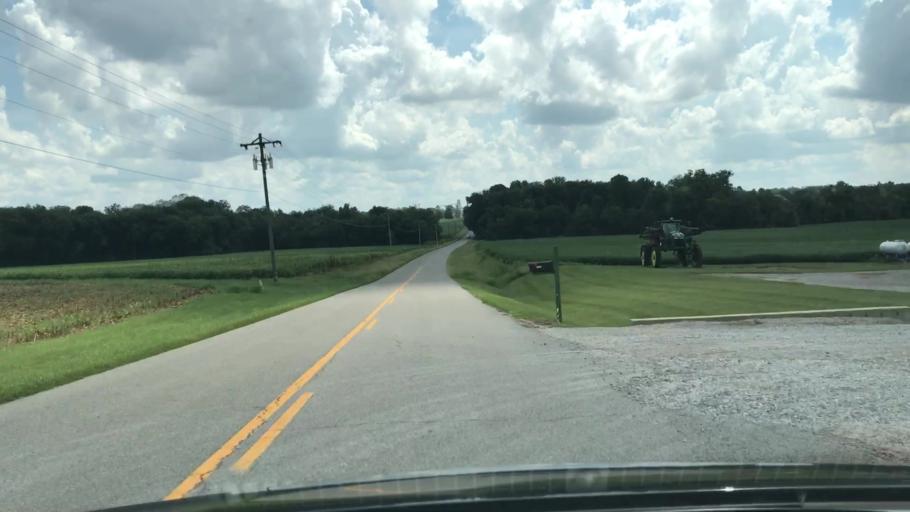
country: US
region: Kentucky
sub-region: Todd County
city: Elkton
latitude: 36.7248
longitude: -87.0859
